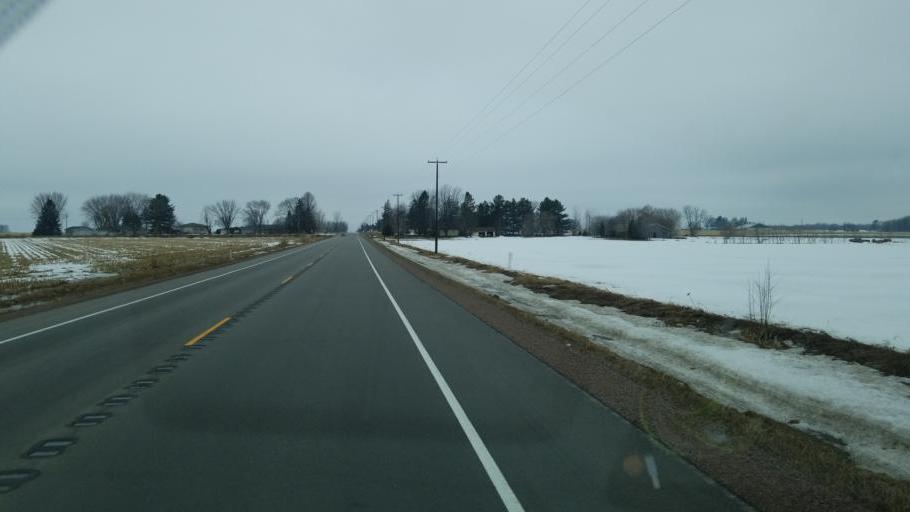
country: US
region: Wisconsin
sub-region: Marathon County
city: Spencer
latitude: 44.6563
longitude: -90.2751
